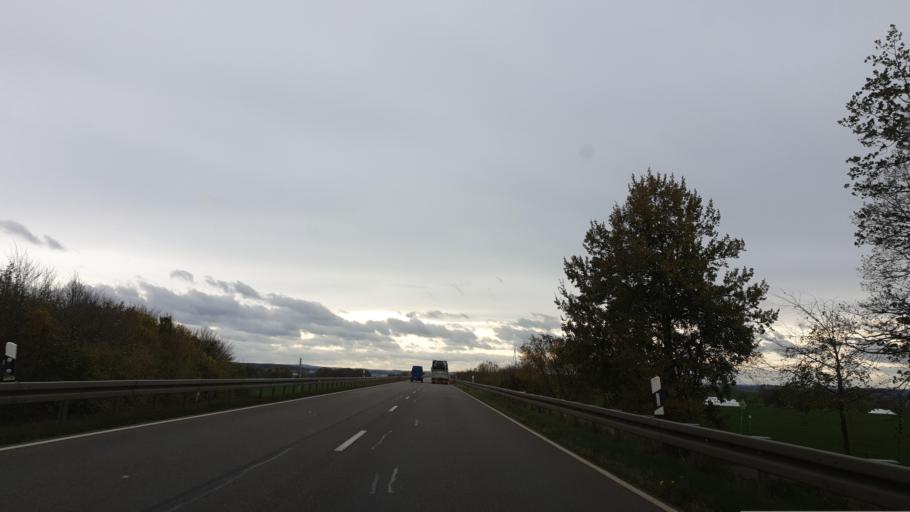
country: DE
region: Saxony
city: Neumark
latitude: 50.6348
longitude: 12.3462
